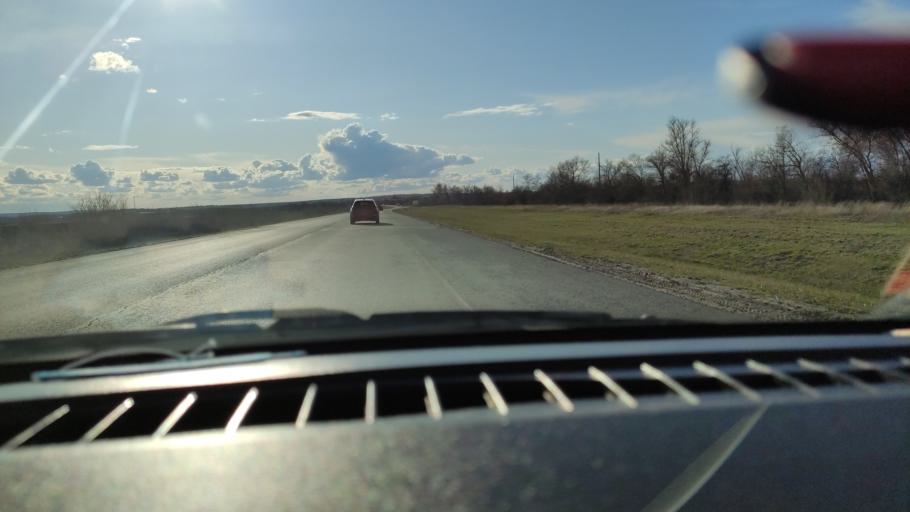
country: RU
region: Saratov
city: Yelshanka
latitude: 51.8303
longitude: 46.2405
